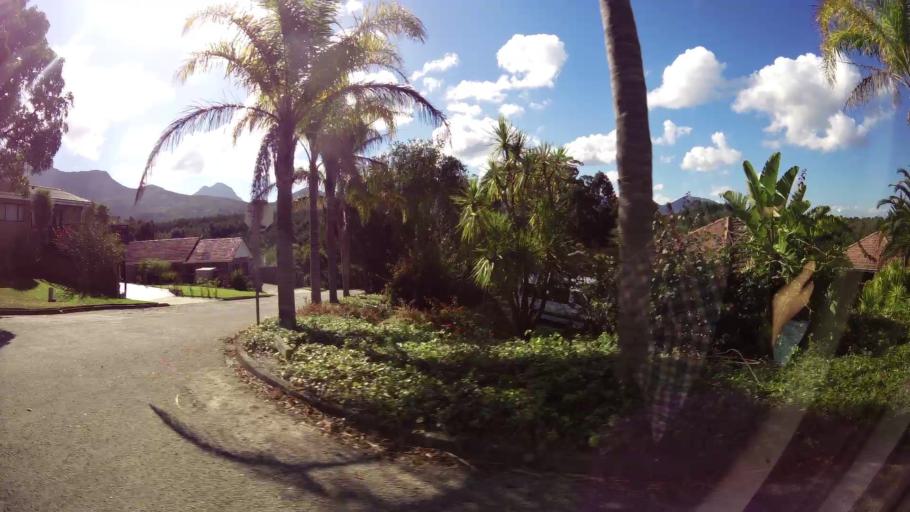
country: ZA
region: Western Cape
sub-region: Eden District Municipality
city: George
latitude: -33.9538
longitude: 22.4826
